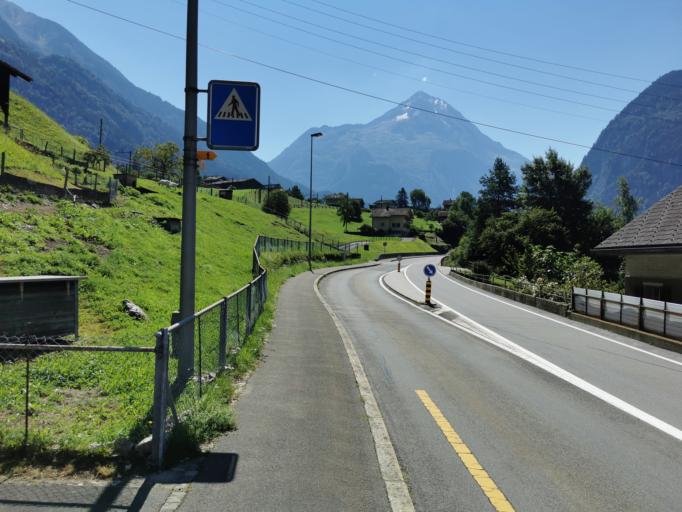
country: CH
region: Uri
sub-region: Uri
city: Erstfeld
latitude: 46.8073
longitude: 8.6647
